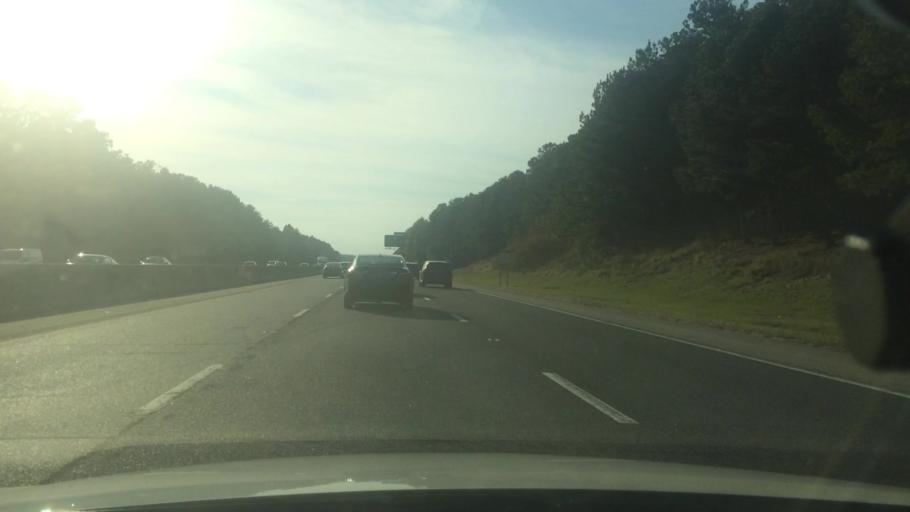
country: US
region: North Carolina
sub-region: Durham County
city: Durham
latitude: 35.9072
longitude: -78.9450
